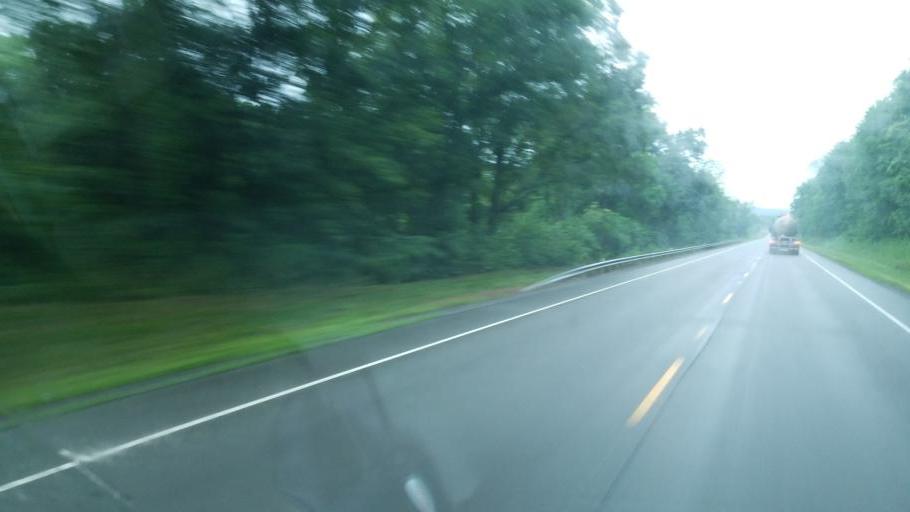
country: US
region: Ohio
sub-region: Coshocton County
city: Coshocton
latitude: 40.2870
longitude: -81.8812
